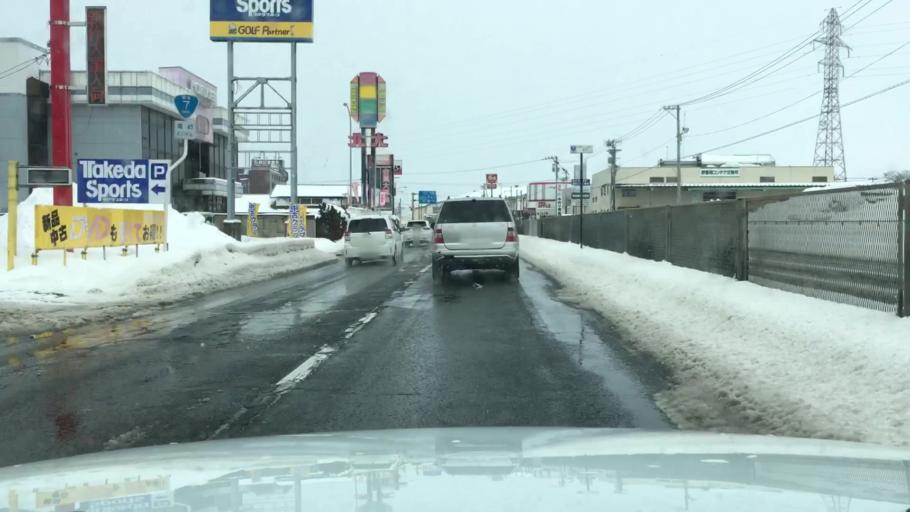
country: JP
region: Aomori
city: Hirosaki
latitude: 40.6082
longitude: 140.4989
